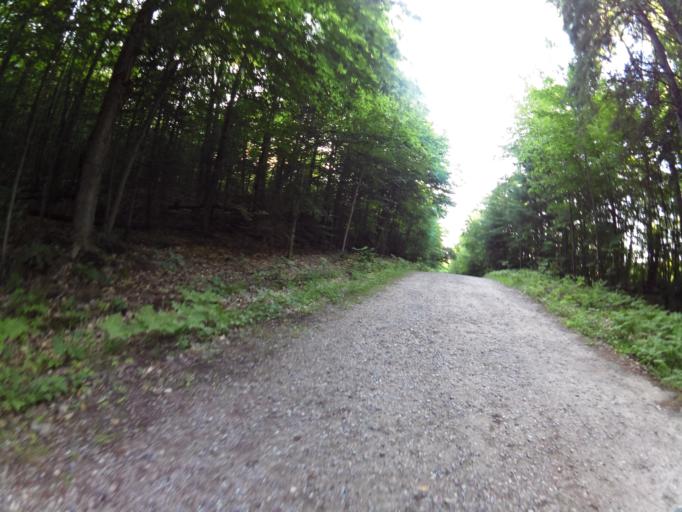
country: CA
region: Quebec
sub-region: Outaouais
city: Wakefield
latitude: 45.5957
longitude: -75.9929
